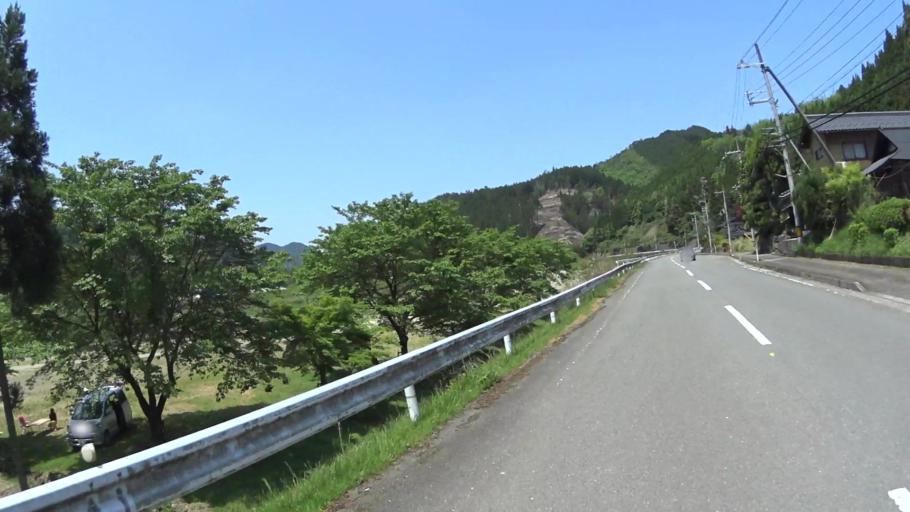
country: JP
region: Kyoto
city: Kameoka
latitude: 35.1355
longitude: 135.6040
